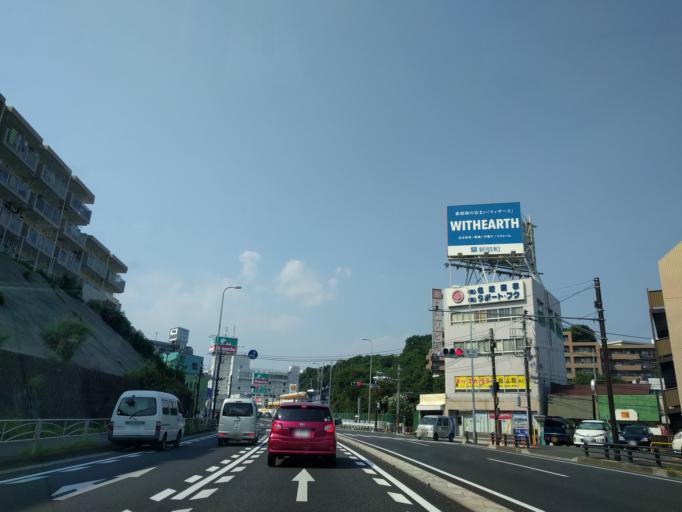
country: JP
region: Kanagawa
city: Yokohama
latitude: 35.4983
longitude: 139.6619
